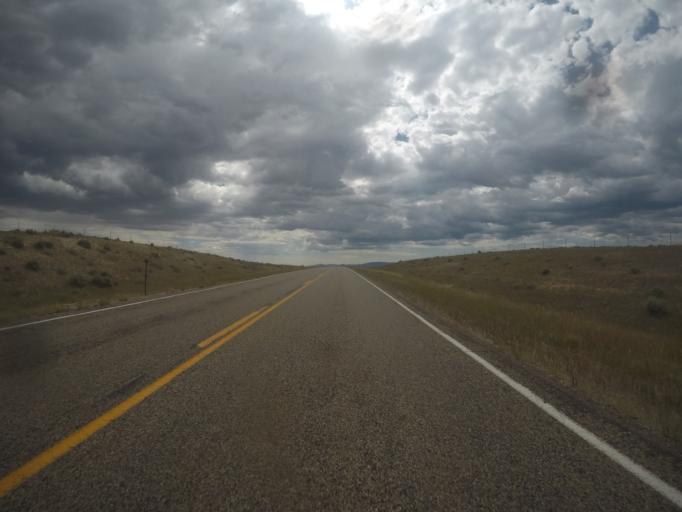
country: US
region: Utah
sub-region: Daggett County
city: Manila
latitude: 41.0167
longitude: -109.8513
